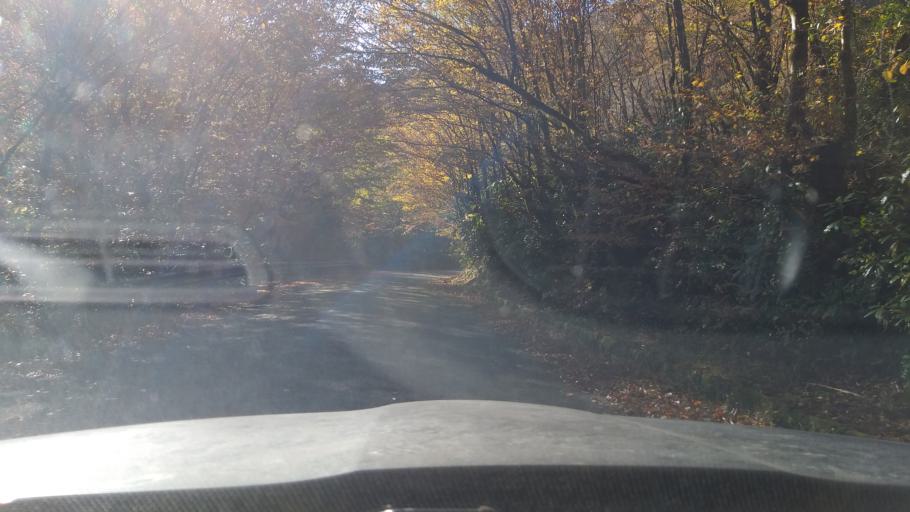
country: GE
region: Abkhazia
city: Bich'vinta
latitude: 43.1892
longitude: 40.4541
